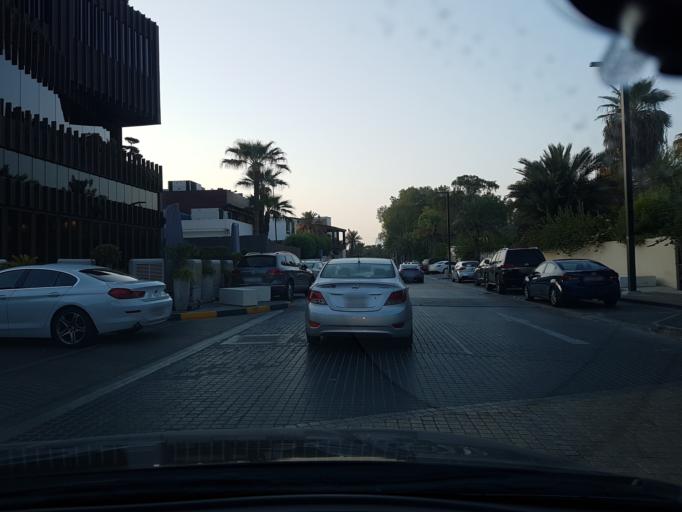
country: BH
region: Manama
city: Manama
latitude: 26.2144
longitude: 50.5930
